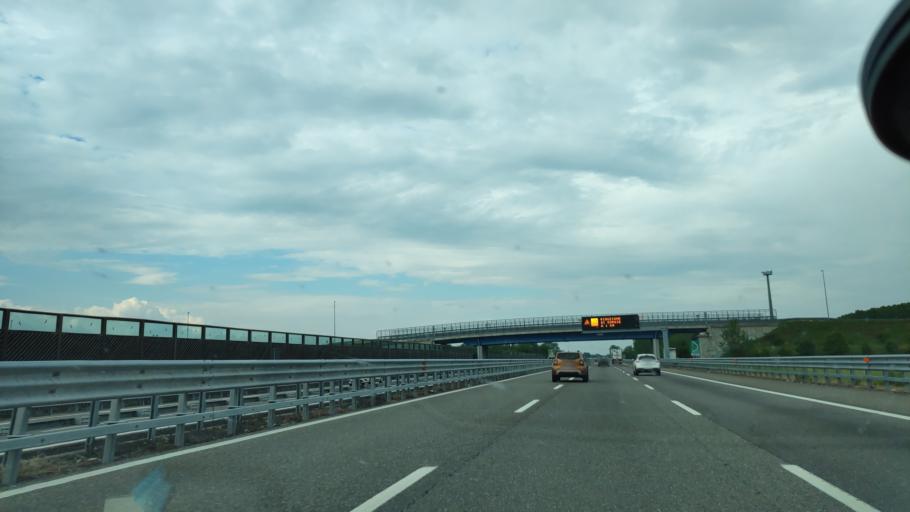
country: IT
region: Lombardy
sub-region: Provincia di Pavia
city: Corana
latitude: 45.0614
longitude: 8.9595
